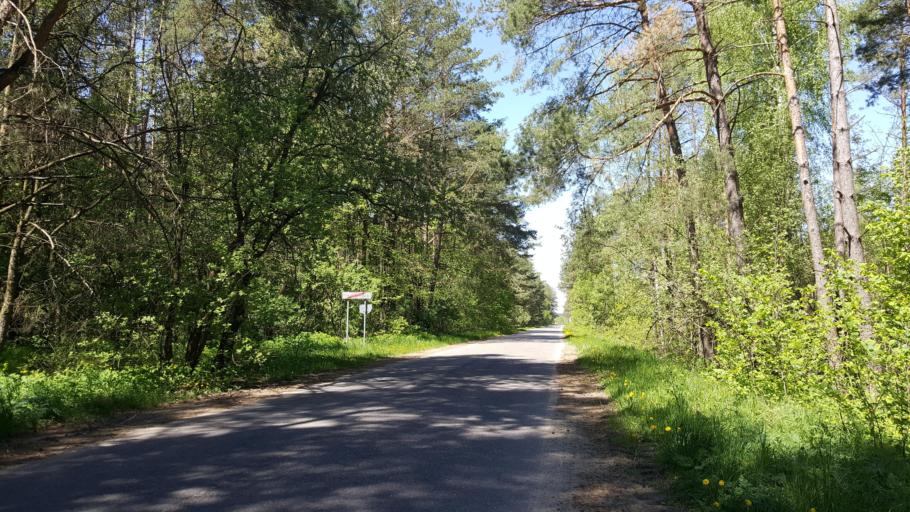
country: BY
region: Brest
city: Kamyanyuki
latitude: 52.5045
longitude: 23.7468
